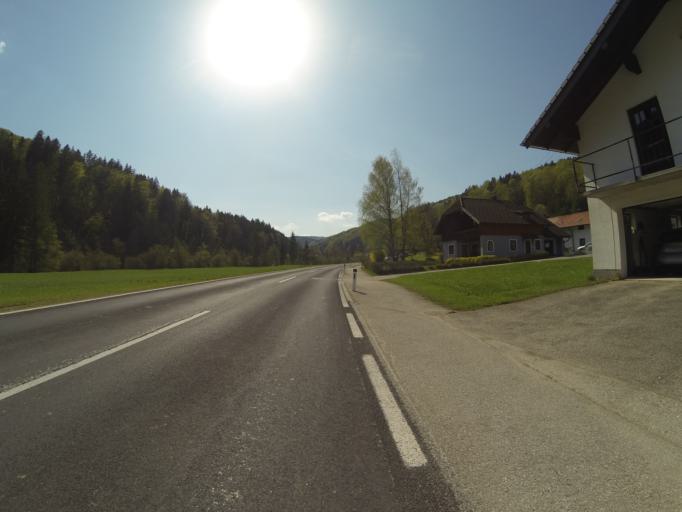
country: AT
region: Upper Austria
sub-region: Politischer Bezirk Gmunden
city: Altmunster
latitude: 47.9186
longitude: 13.7311
